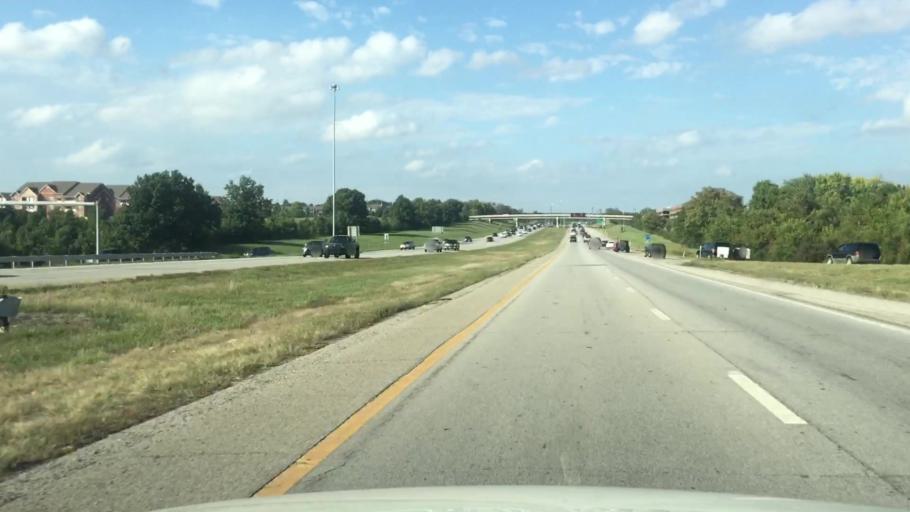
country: US
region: Kansas
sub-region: Johnson County
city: Lenexa
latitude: 38.8855
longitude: -94.6763
